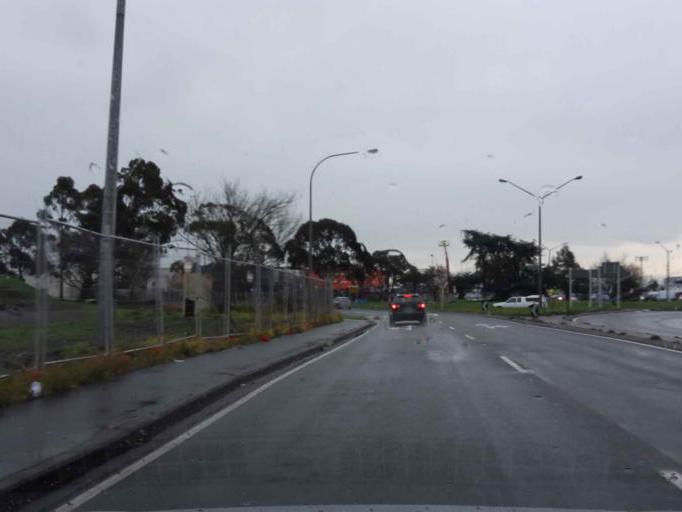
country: NZ
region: Canterbury
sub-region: Selwyn District
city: Prebbleton
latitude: -43.5393
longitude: 172.5555
